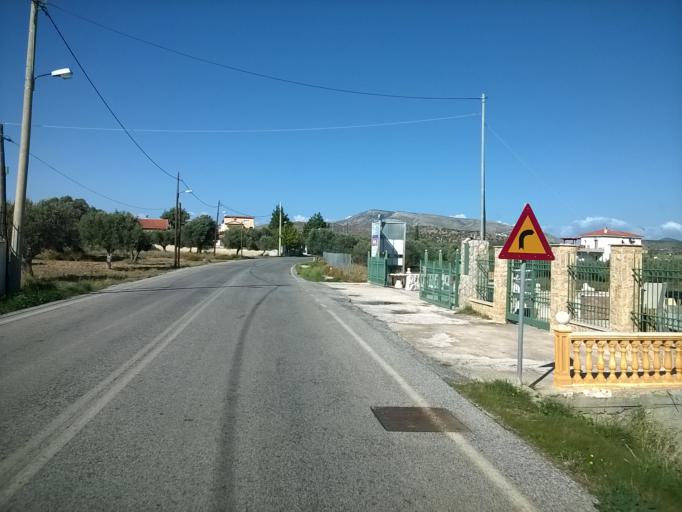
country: GR
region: Attica
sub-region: Nomarchia Anatolikis Attikis
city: Keratea
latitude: 37.7952
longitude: 23.9985
